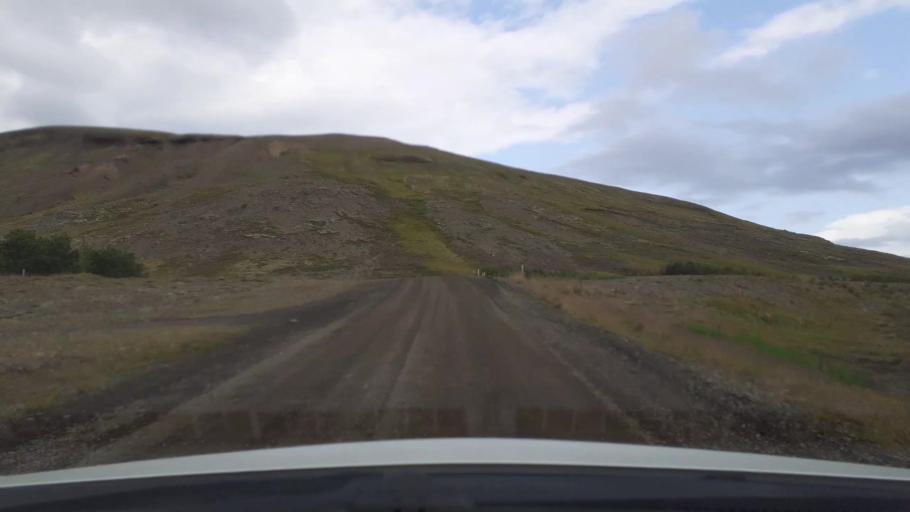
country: IS
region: Capital Region
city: Mosfellsbaer
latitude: 64.2956
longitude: -21.6631
